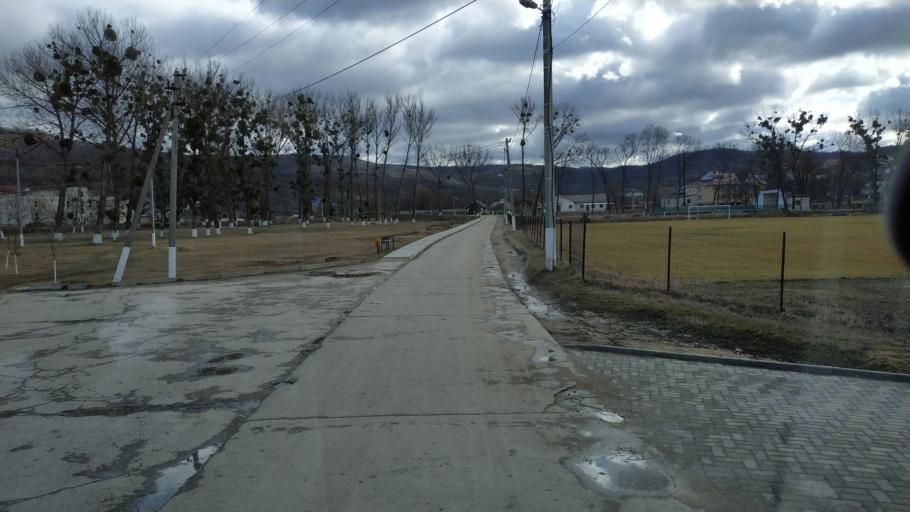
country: MD
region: Stinga Nistrului
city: Bucovat
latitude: 47.1349
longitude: 28.3833
